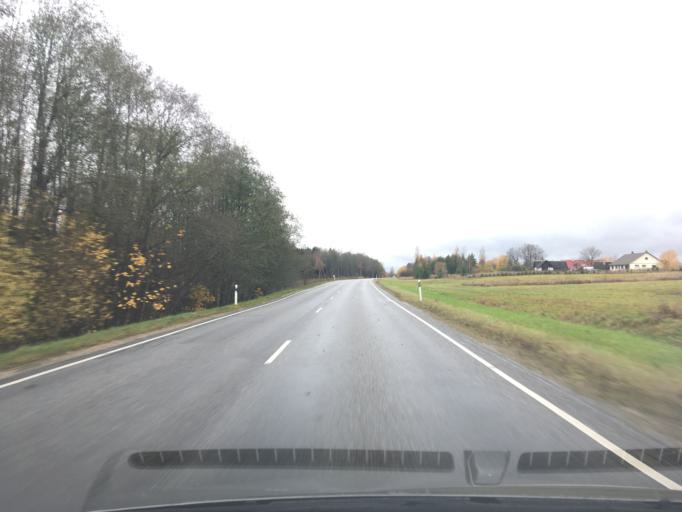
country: EE
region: Jogevamaa
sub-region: Tabivere vald
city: Tabivere
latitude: 58.4668
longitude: 26.5777
